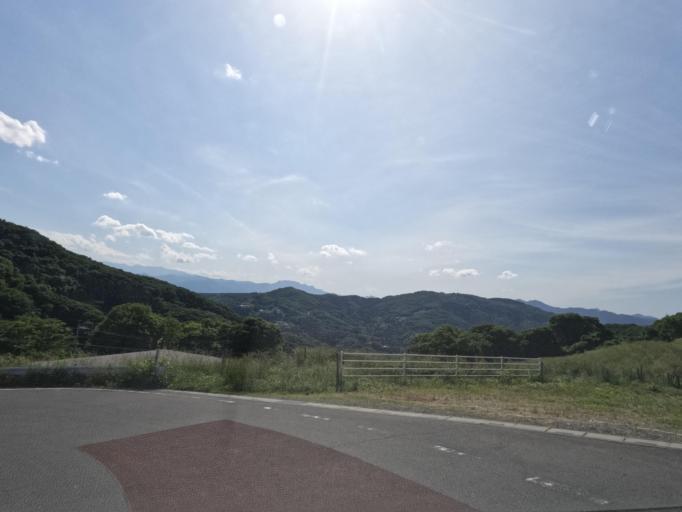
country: JP
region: Saitama
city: Yorii
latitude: 36.0495
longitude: 139.1493
